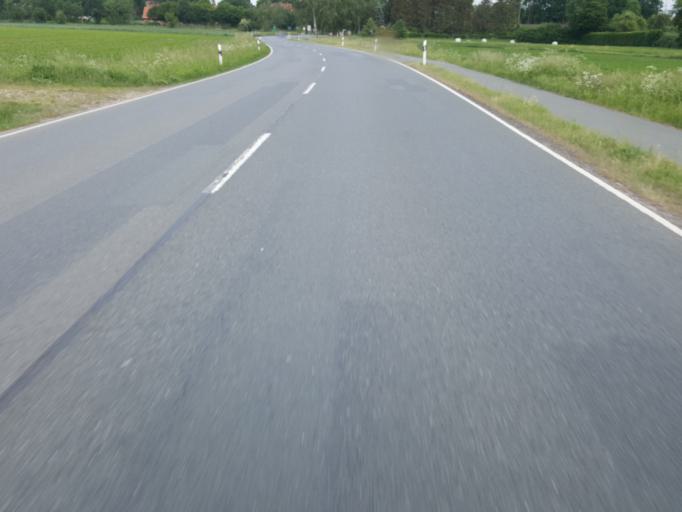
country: DE
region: Lower Saxony
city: Leese
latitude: 52.5078
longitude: 9.1028
